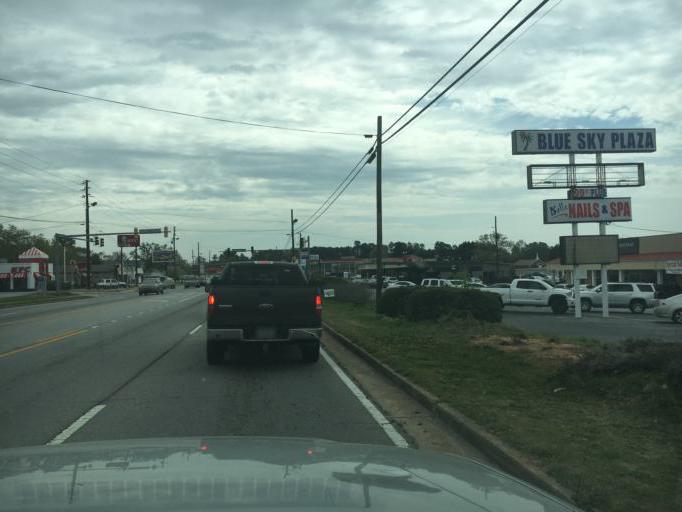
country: US
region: Georgia
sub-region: Stephens County
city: Toccoa
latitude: 34.5738
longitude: -83.3122
